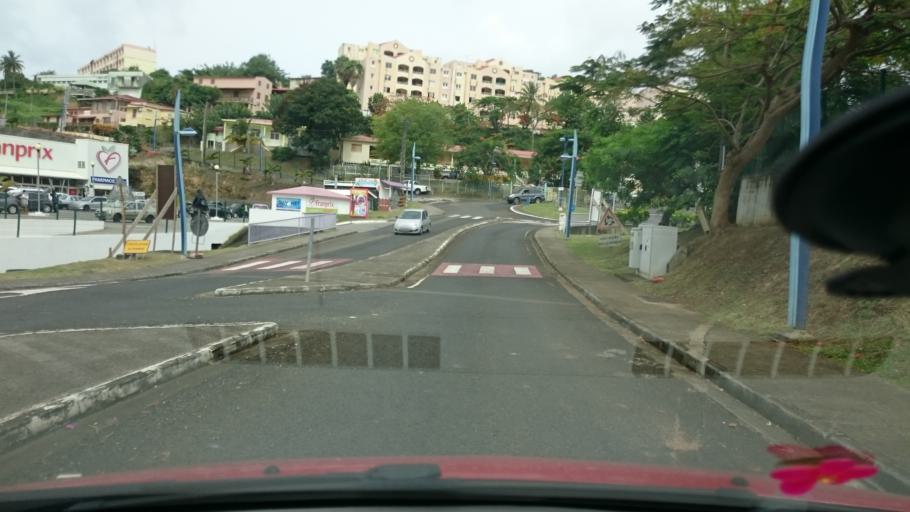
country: MQ
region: Martinique
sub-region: Martinique
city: Riviere-Pilote
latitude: 14.4825
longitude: -60.9049
